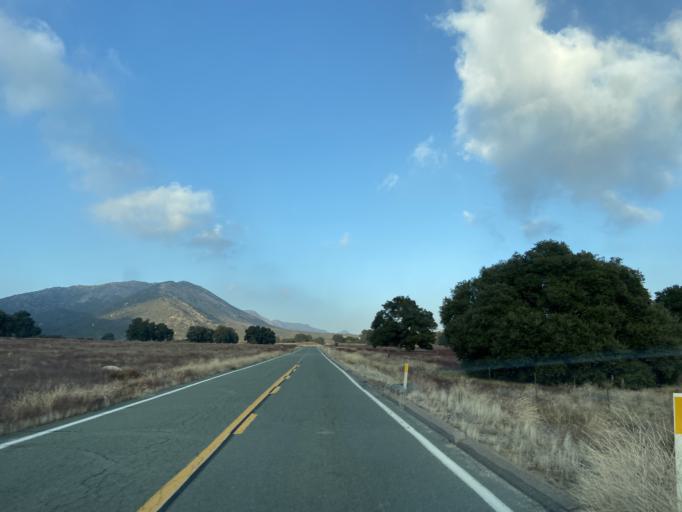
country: US
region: California
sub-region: San Diego County
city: Campo
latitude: 32.7226
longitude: -116.4668
